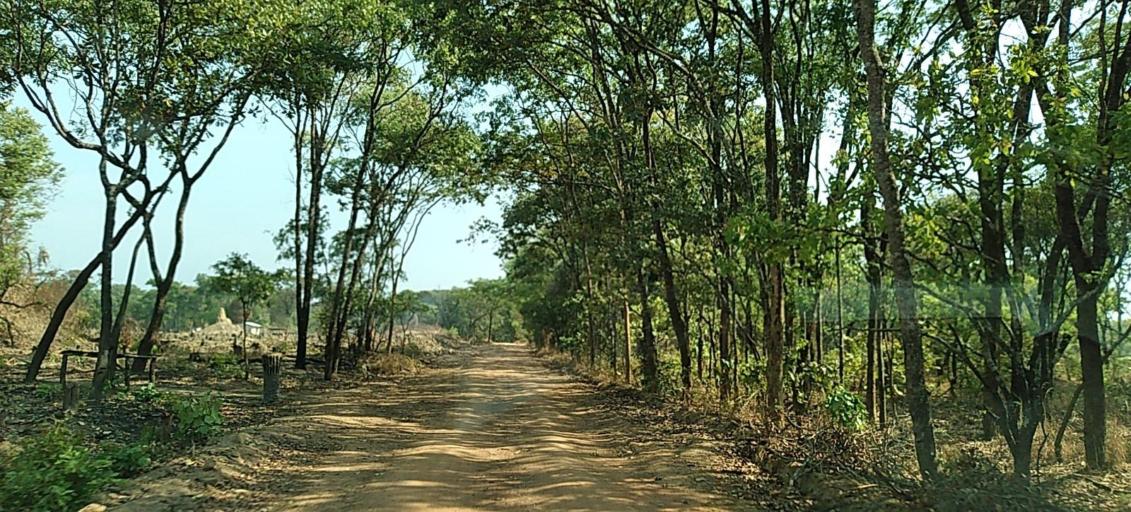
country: ZM
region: Copperbelt
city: Kalulushi
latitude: -12.9247
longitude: 27.8221
